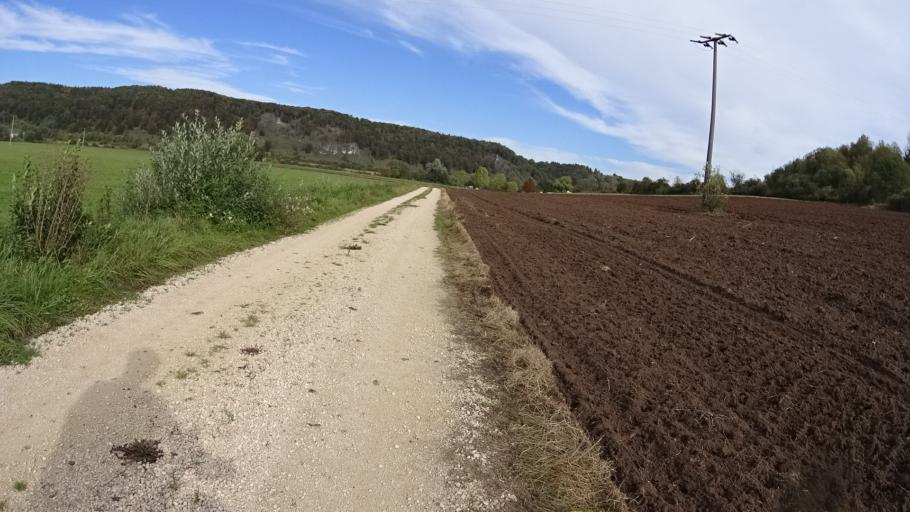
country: DE
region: Bavaria
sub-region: Upper Bavaria
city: Walting
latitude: 48.9324
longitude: 11.3168
